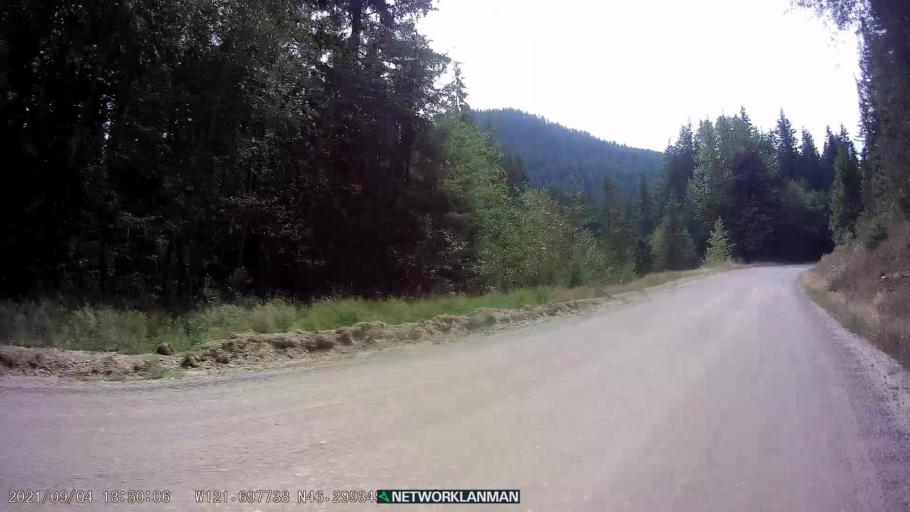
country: US
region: Washington
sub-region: Skamania County
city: Carson
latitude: 46.2992
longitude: -121.6980
